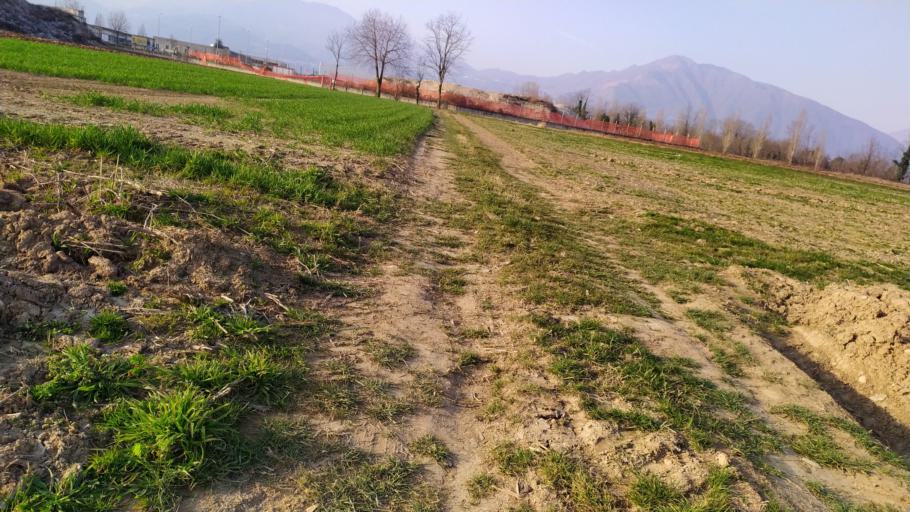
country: IT
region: Veneto
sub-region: Provincia di Vicenza
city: San Vito di Leguzzano
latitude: 45.6838
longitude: 11.4058
